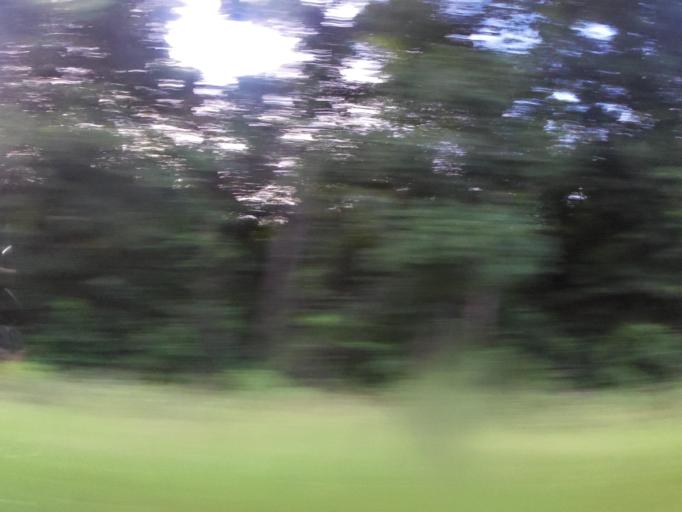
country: US
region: Florida
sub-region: Duval County
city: Jacksonville
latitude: 30.4137
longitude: -81.6112
